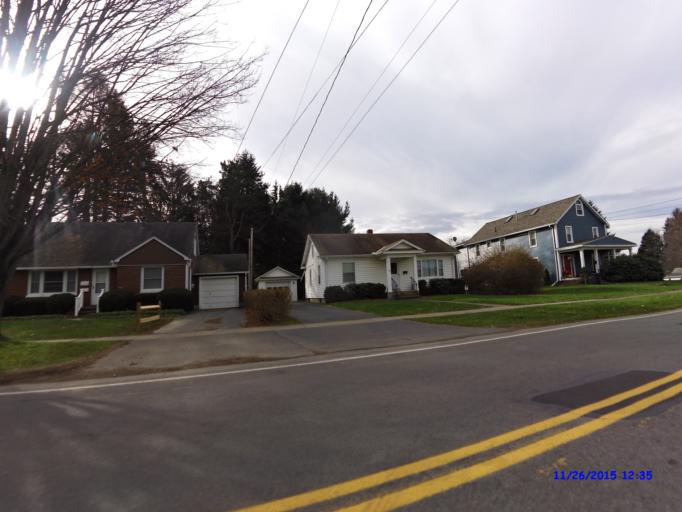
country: US
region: New York
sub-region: Cattaraugus County
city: Allegany
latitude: 42.0852
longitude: -78.4898
